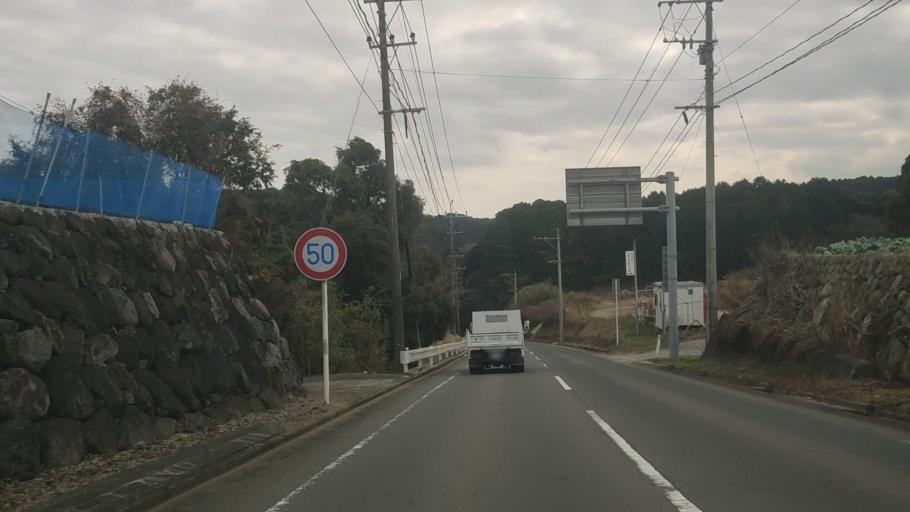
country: JP
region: Nagasaki
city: Shimabara
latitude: 32.8527
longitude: 130.2622
